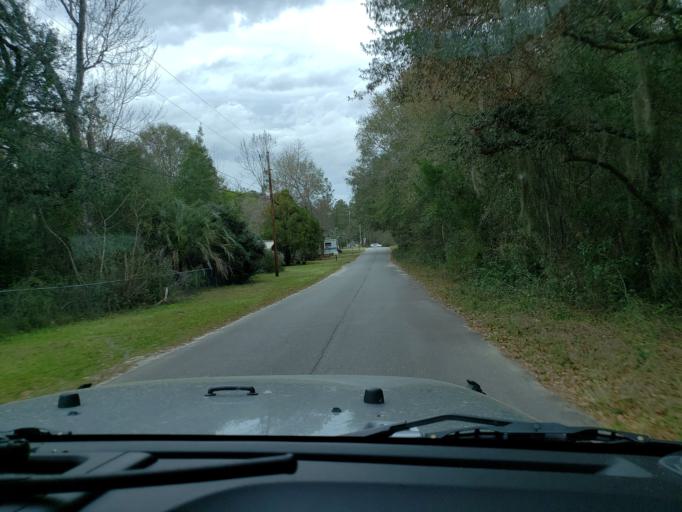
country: US
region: Georgia
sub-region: Chatham County
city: Bloomingdale
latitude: 32.0764
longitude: -81.3698
